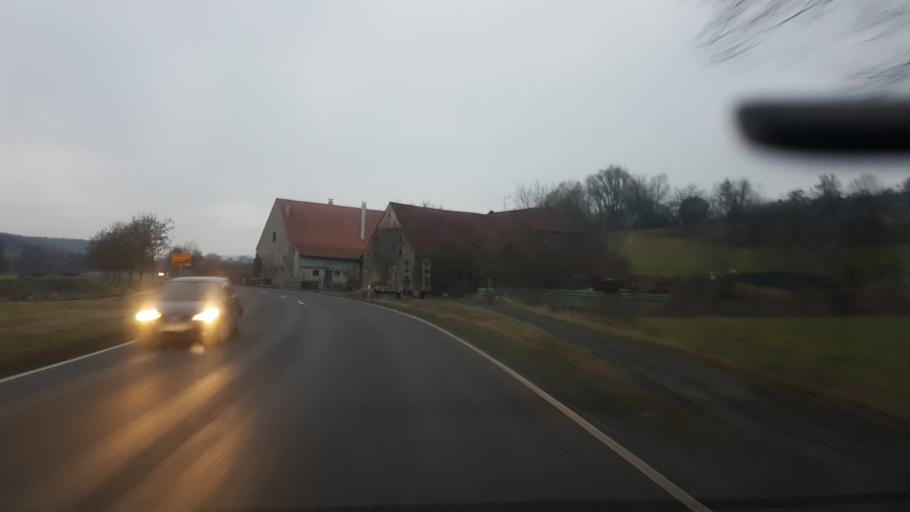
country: DE
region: Bavaria
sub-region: Regierungsbezirk Unterfranken
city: Pfarrweisach
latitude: 50.1623
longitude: 10.7265
